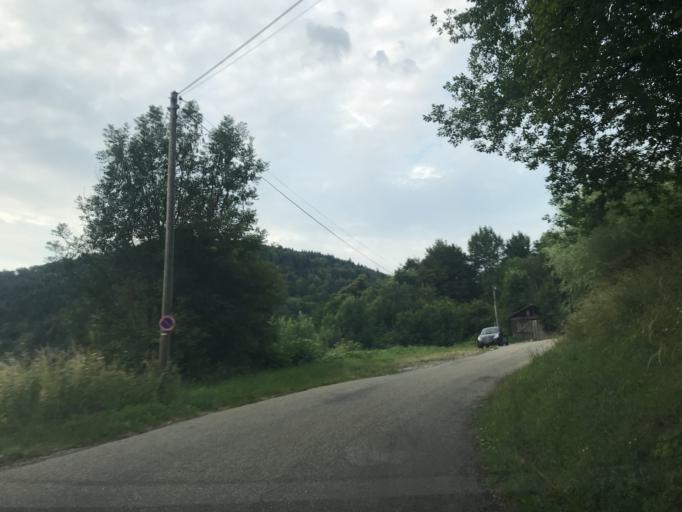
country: FR
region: Rhone-Alpes
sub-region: Departement de l'Isere
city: Saint-Vincent-de-Mercuze
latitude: 45.3898
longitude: 5.9332
